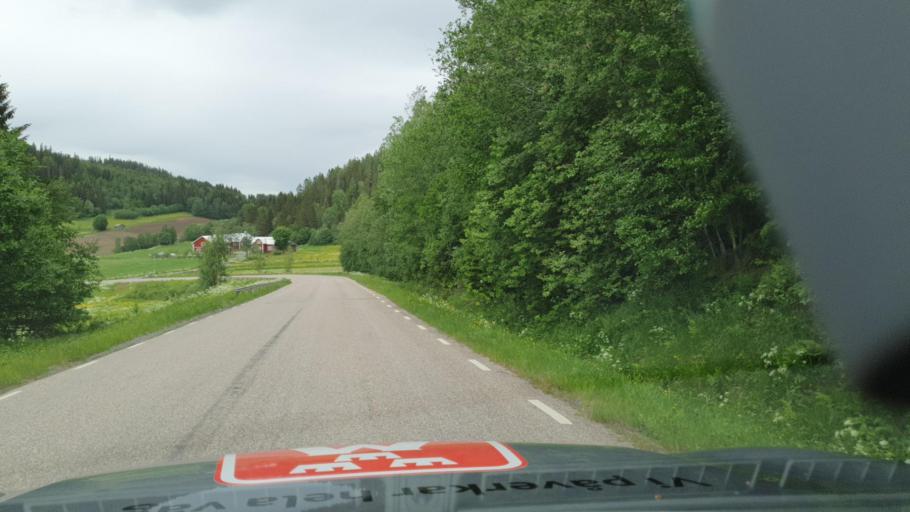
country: SE
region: Vaesternorrland
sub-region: Kramfors Kommun
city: Nordingra
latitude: 62.9007
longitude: 18.3677
